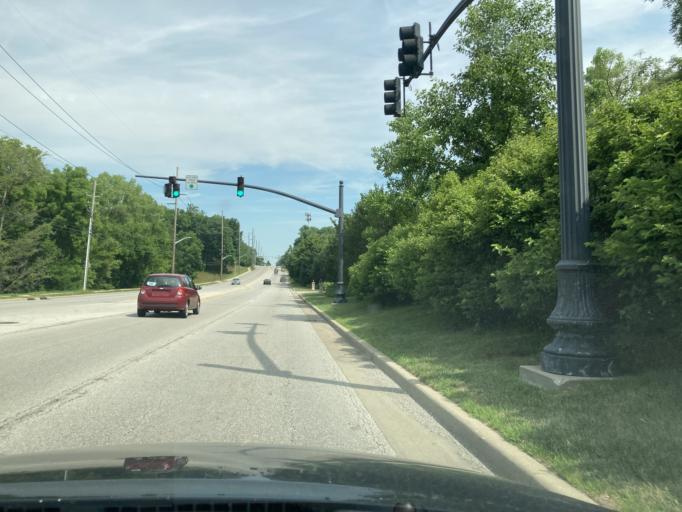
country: US
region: Indiana
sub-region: Marion County
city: Broad Ripple
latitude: 39.8357
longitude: -86.1859
